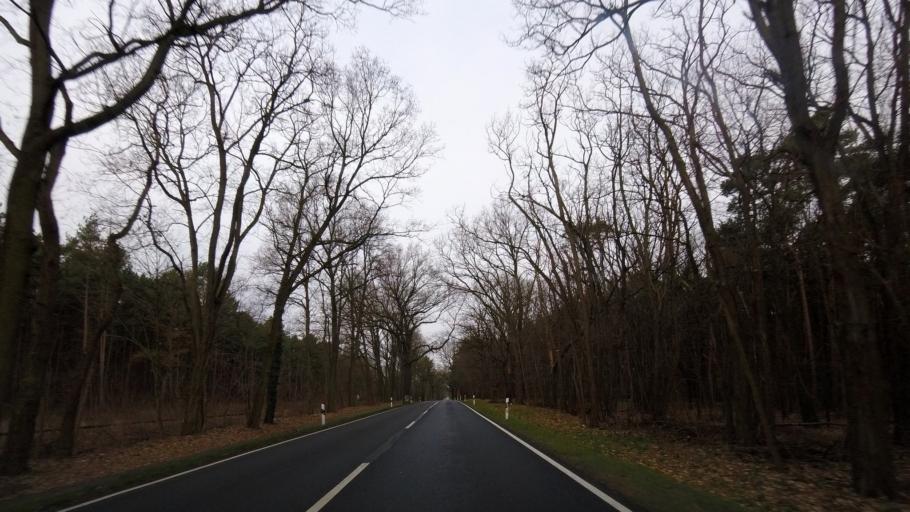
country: DE
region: Brandenburg
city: Treuenbrietzen
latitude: 52.0761
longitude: 12.8848
